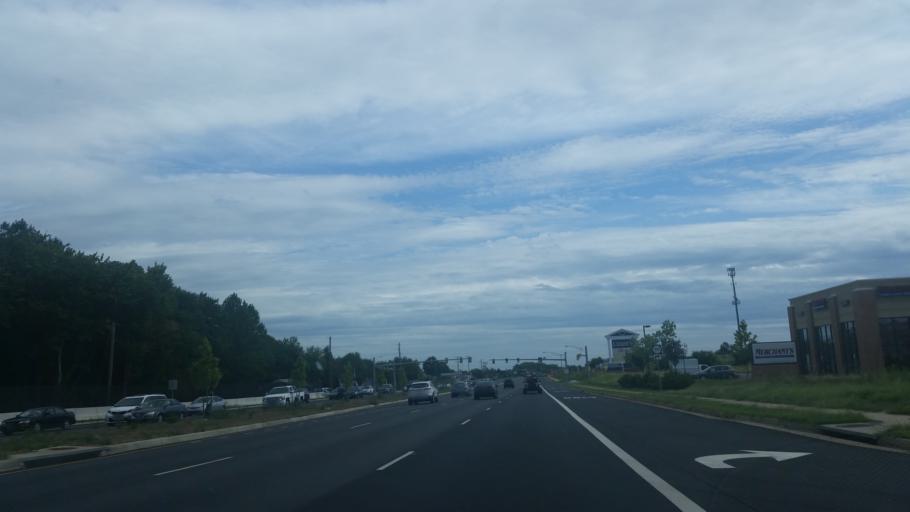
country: US
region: Virginia
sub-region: Stafford County
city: Falmouth
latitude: 38.3580
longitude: -77.5165
